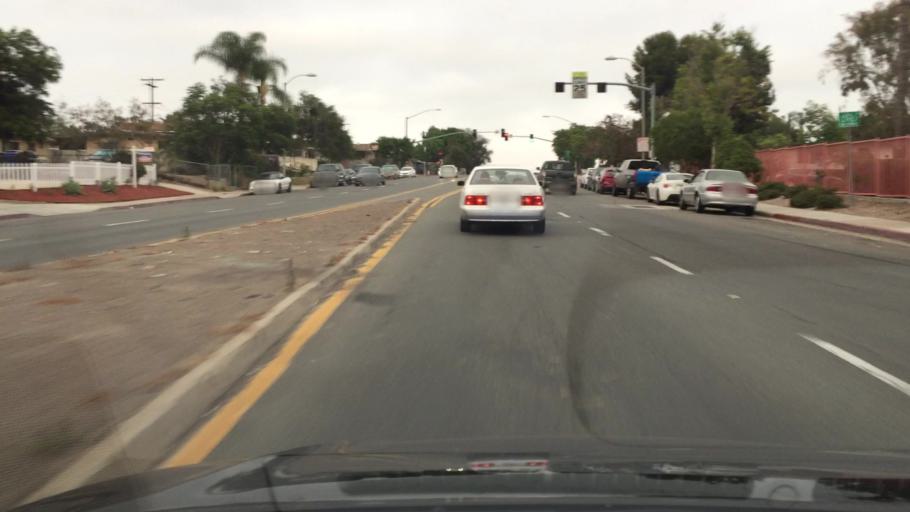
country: US
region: California
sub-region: San Diego County
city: National City
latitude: 32.7114
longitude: -117.0996
